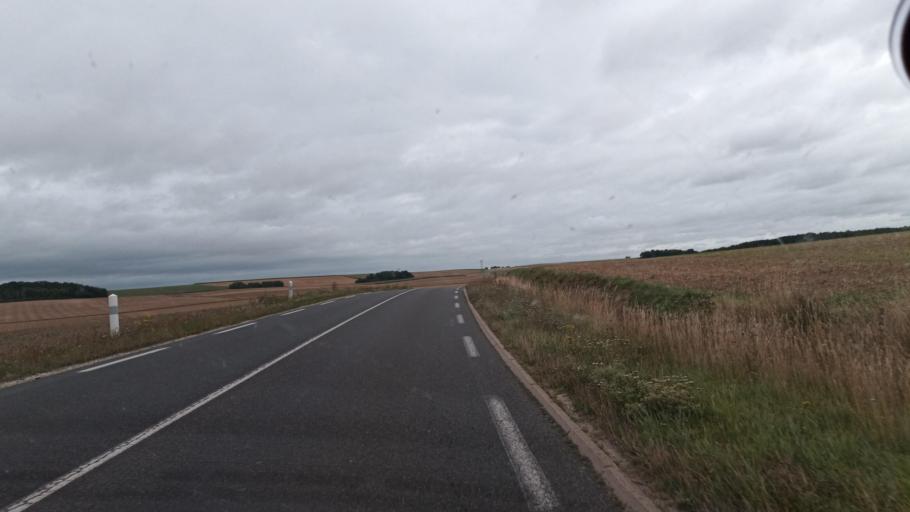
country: FR
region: Ile-de-France
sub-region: Departement de Seine-et-Marne
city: Voulx
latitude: 48.3132
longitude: 2.9480
